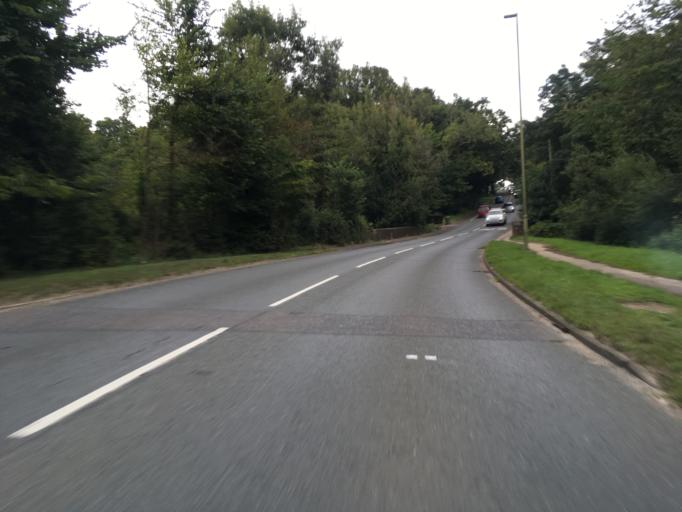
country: GB
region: England
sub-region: Hampshire
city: Petersfield
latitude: 51.0147
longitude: -0.9161
